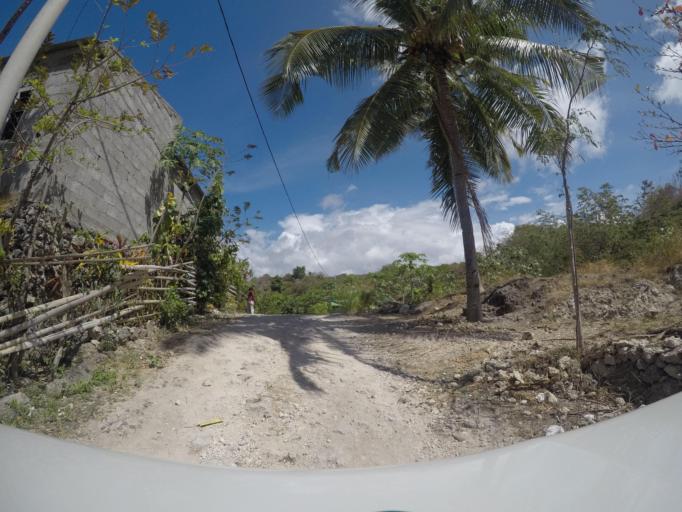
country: TL
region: Baucau
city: Baucau
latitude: -8.4477
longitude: 126.4379
